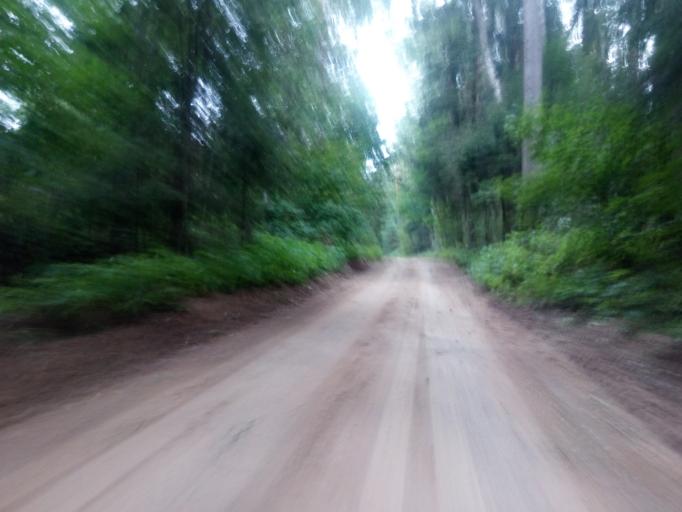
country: BY
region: Vitebsk
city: Dzisna
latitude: 55.7051
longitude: 28.3364
